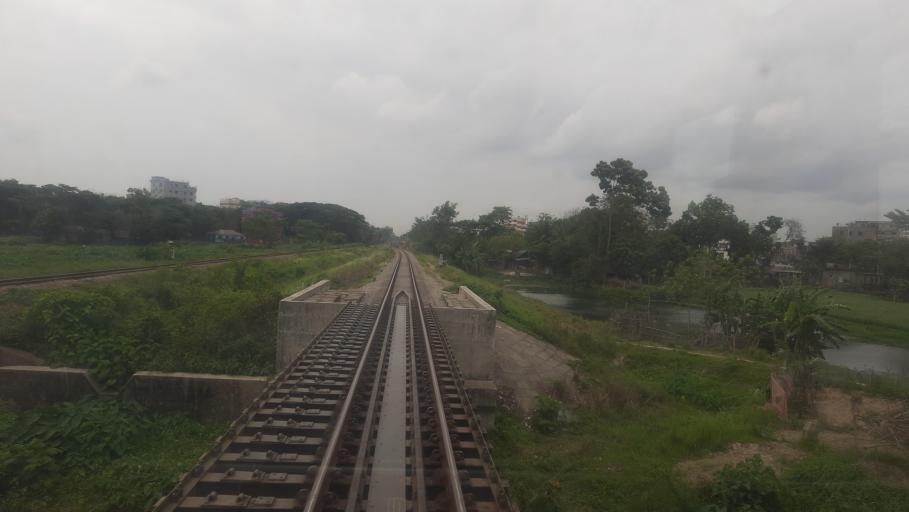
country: BD
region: Chittagong
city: Feni
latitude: 23.0077
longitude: 91.4118
